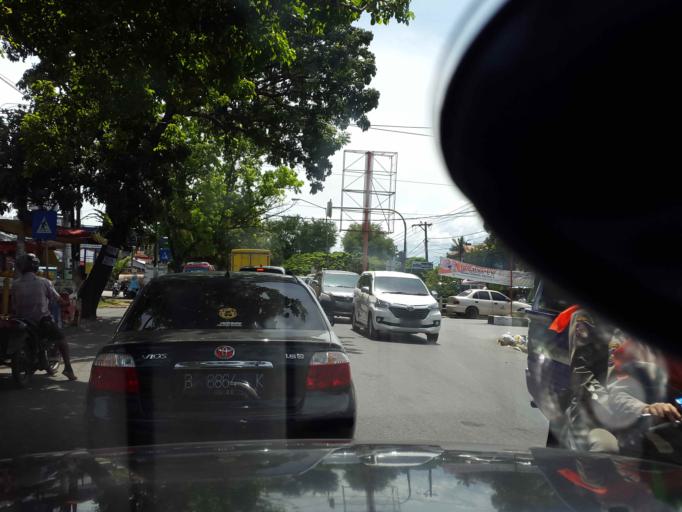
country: ID
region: West Sumatra
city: Padang
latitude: -0.9438
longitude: 100.3664
